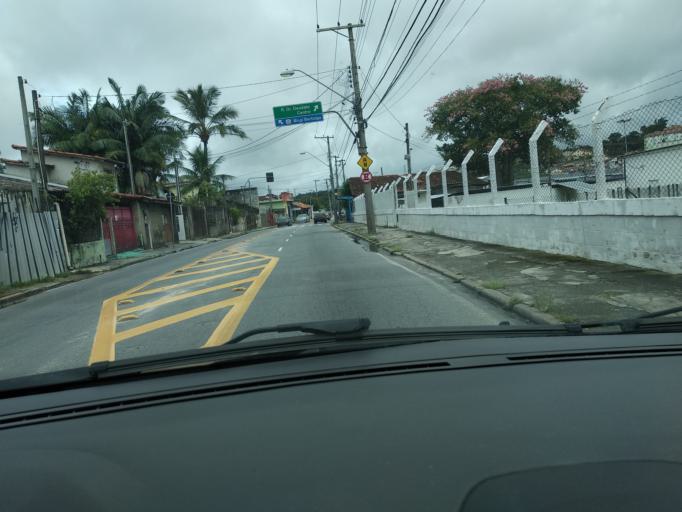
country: BR
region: Sao Paulo
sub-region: Mogi das Cruzes
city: Mogi das Cruzes
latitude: -23.5436
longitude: -46.1837
